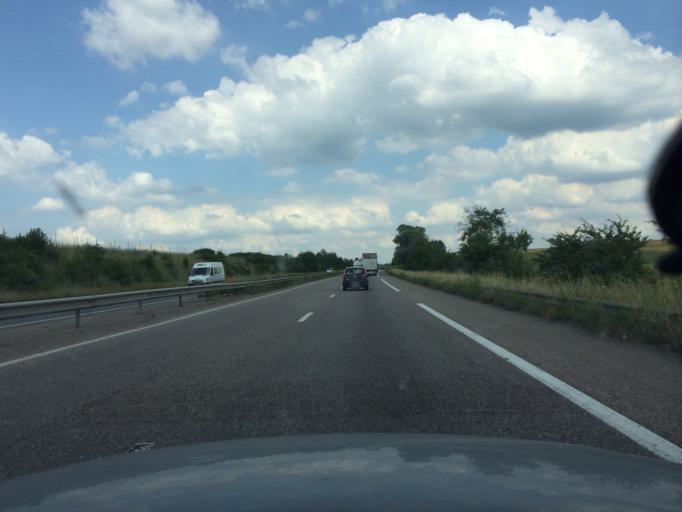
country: FR
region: Lorraine
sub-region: Departement de Meurthe-et-Moselle
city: Gondreville
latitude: 48.6882
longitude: 5.9663
